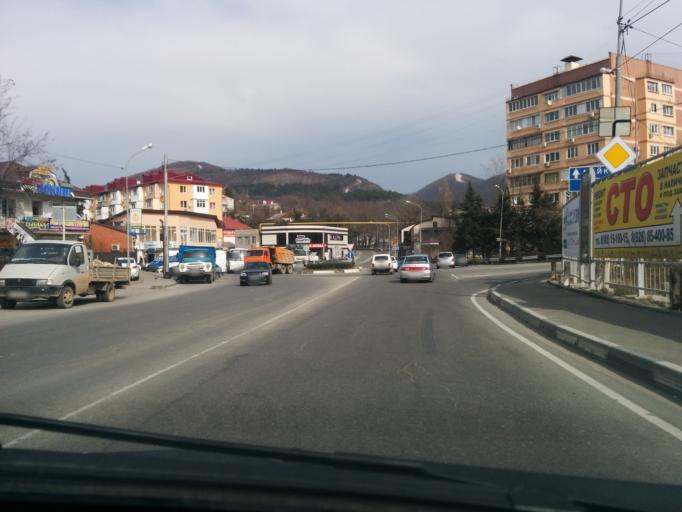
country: RU
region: Krasnodarskiy
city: Tuapse
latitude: 44.1054
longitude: 39.0867
